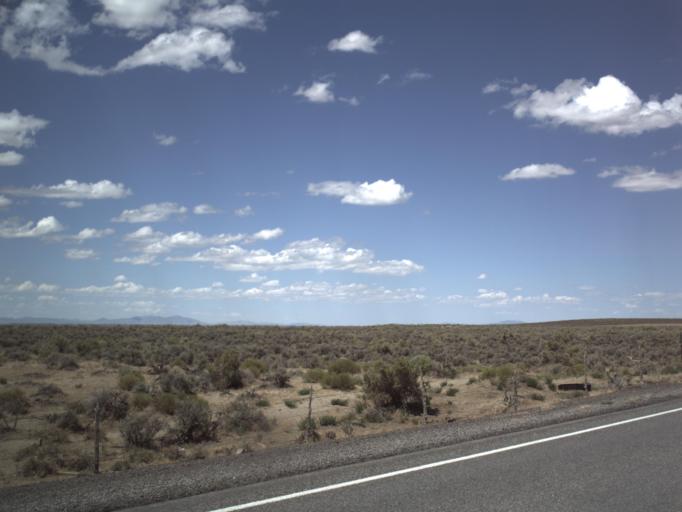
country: US
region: Utah
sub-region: Millard County
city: Fillmore
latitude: 39.1657
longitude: -112.4100
